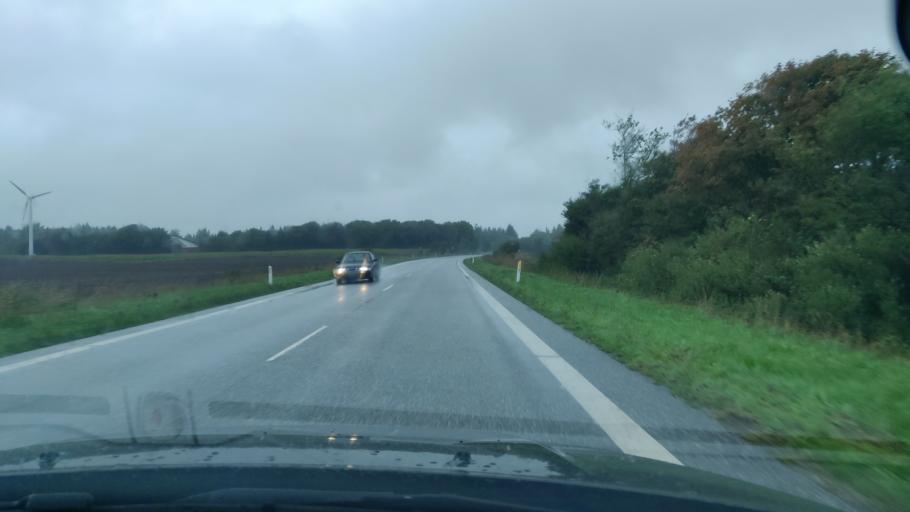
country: DK
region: North Denmark
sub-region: Thisted Kommune
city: Hurup
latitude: 56.8327
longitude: 8.5070
